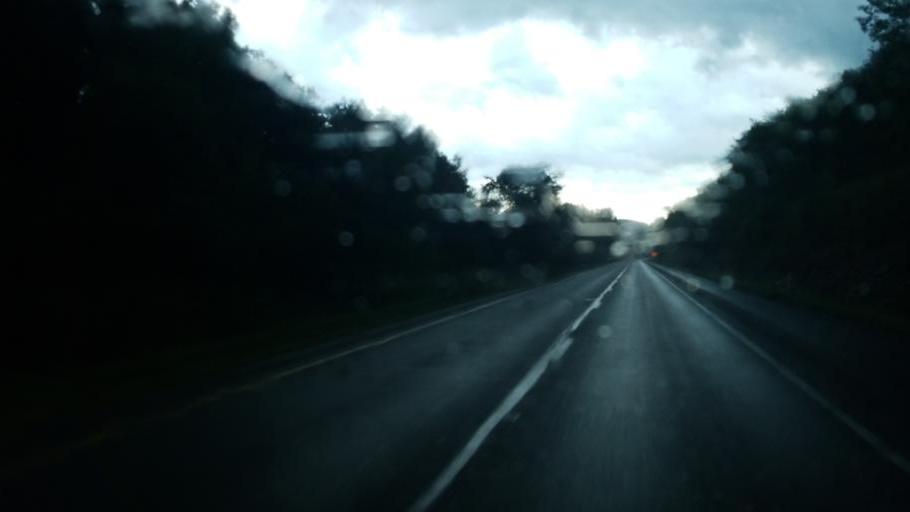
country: US
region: Pennsylvania
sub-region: Butler County
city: Prospect
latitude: 40.8857
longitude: -80.1178
